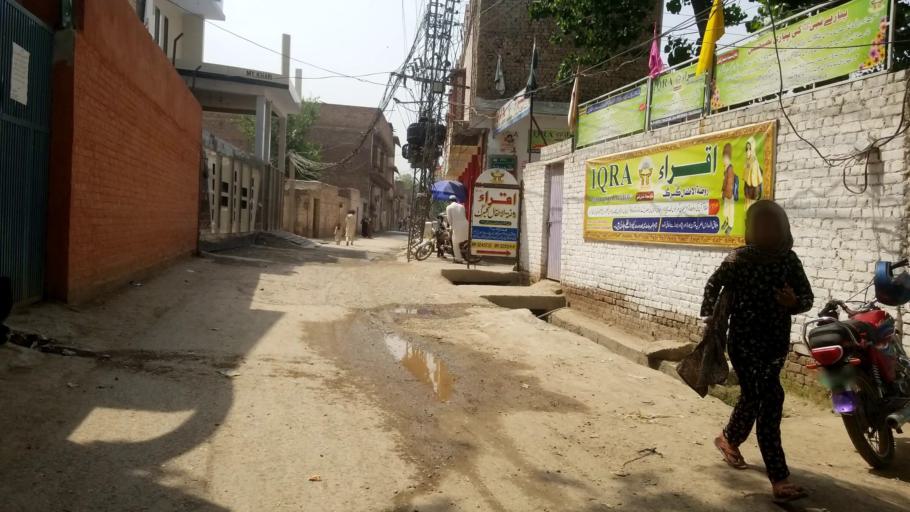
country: PK
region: Khyber Pakhtunkhwa
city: Peshawar
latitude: 33.9860
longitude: 71.5402
